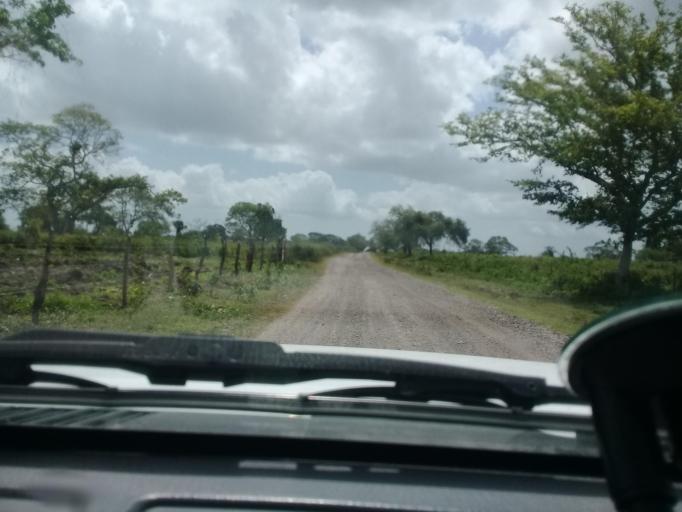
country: MX
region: Veracruz
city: Moralillo
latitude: 22.1598
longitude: -97.9949
